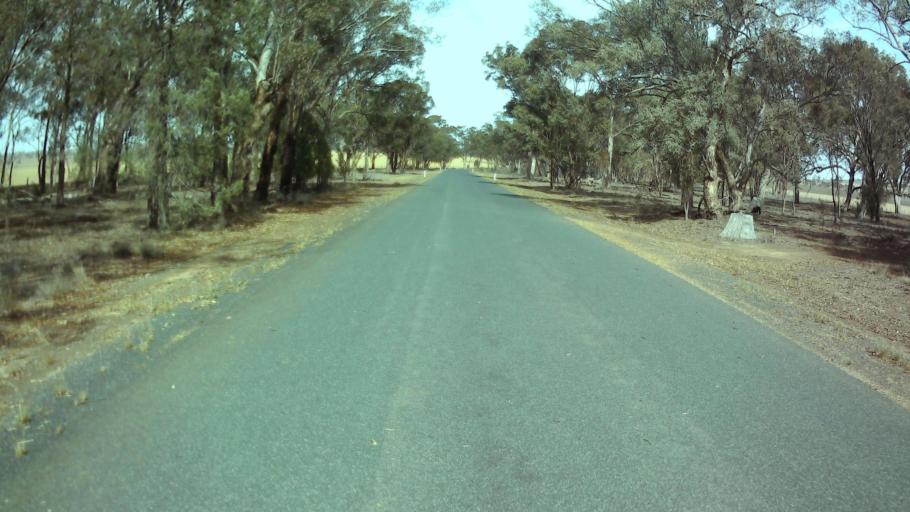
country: AU
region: New South Wales
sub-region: Weddin
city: Grenfell
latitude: -33.8087
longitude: 148.0695
